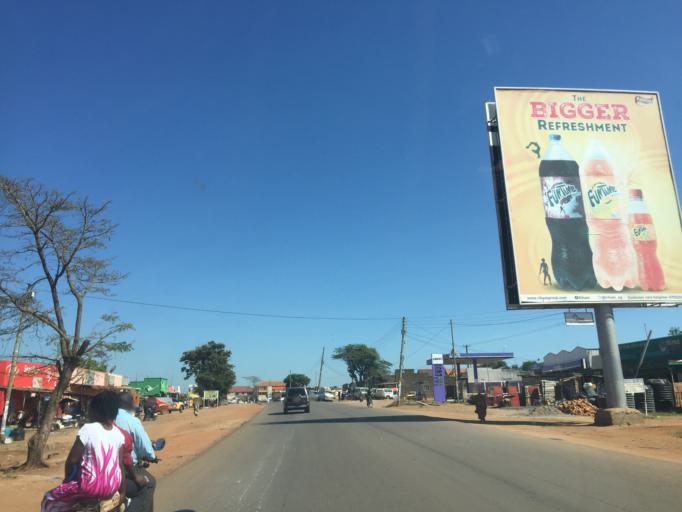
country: UG
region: Central Region
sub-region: Luwero District
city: Luwero
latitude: 0.8283
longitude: 32.5017
